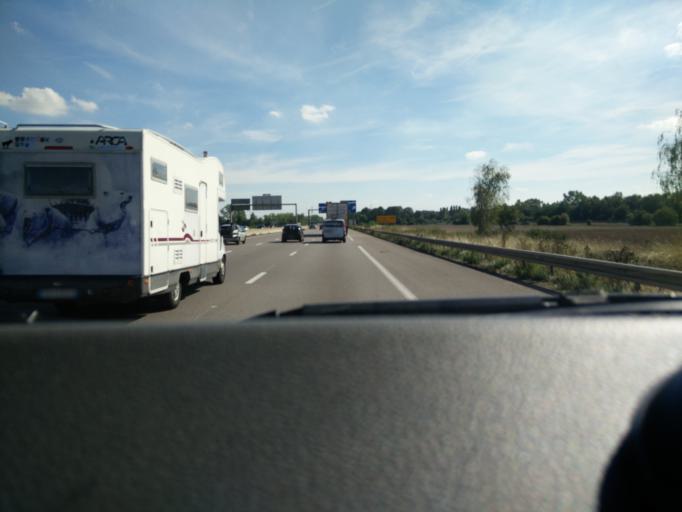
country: FR
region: Lorraine
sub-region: Departement de la Moselle
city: Maizieres-les-Metz
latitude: 49.2110
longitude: 6.1746
